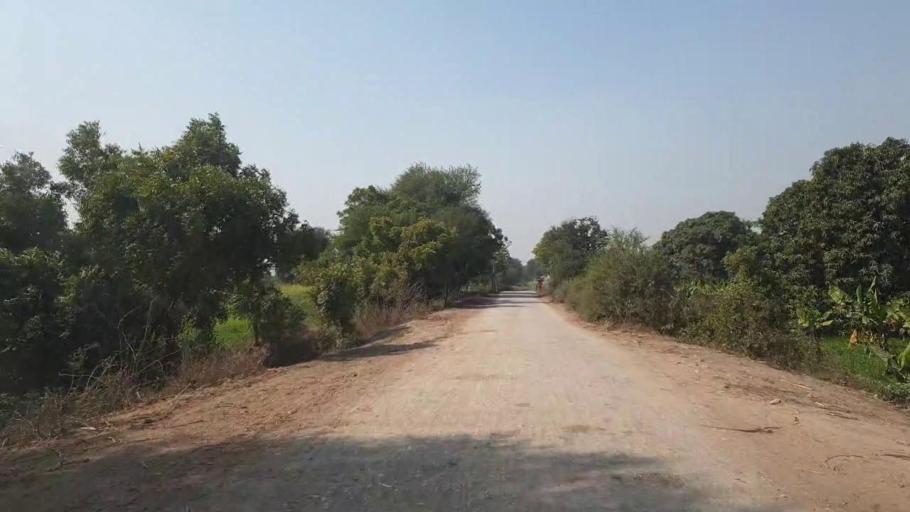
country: PK
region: Sindh
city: Tando Jam
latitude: 25.3299
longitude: 68.6230
